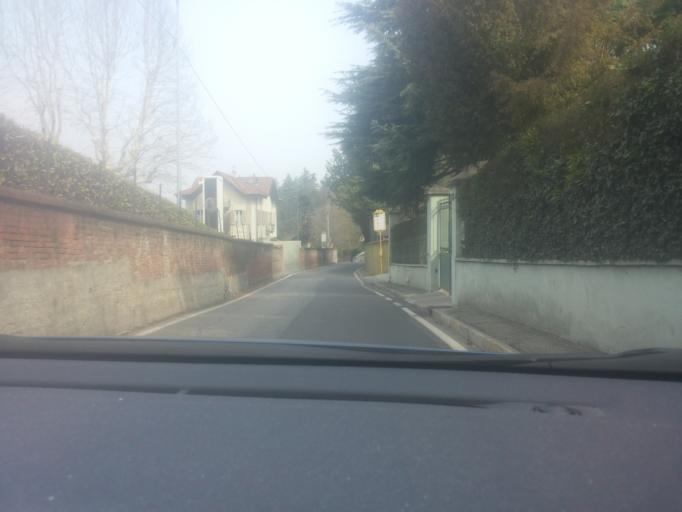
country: IT
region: Piedmont
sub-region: Provincia di Torino
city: Turin
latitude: 45.0619
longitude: 7.7156
